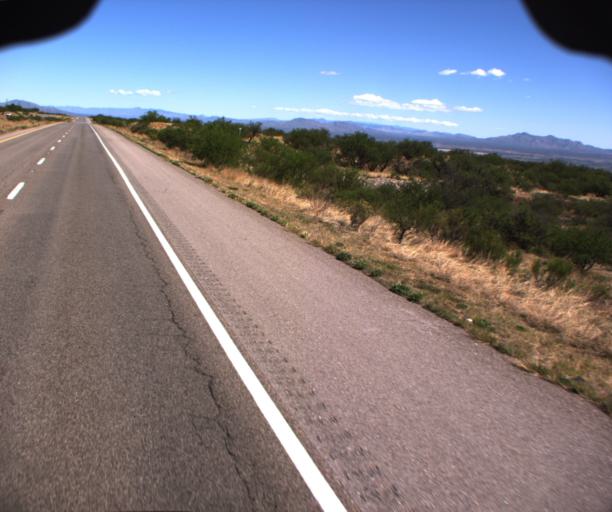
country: US
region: Arizona
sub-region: Cochise County
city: Whetstone
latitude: 31.8755
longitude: -110.3410
